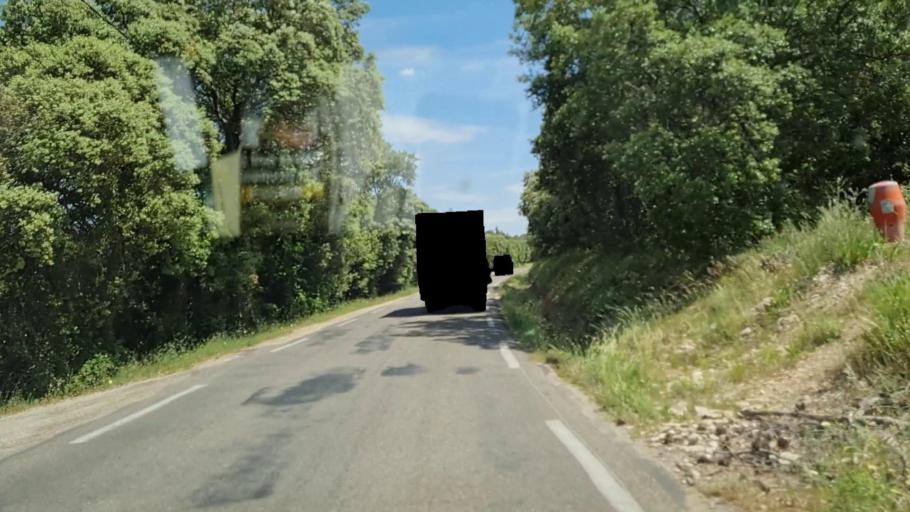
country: FR
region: Languedoc-Roussillon
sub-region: Departement du Gard
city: Saint-Gervasy
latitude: 43.8841
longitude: 4.4685
